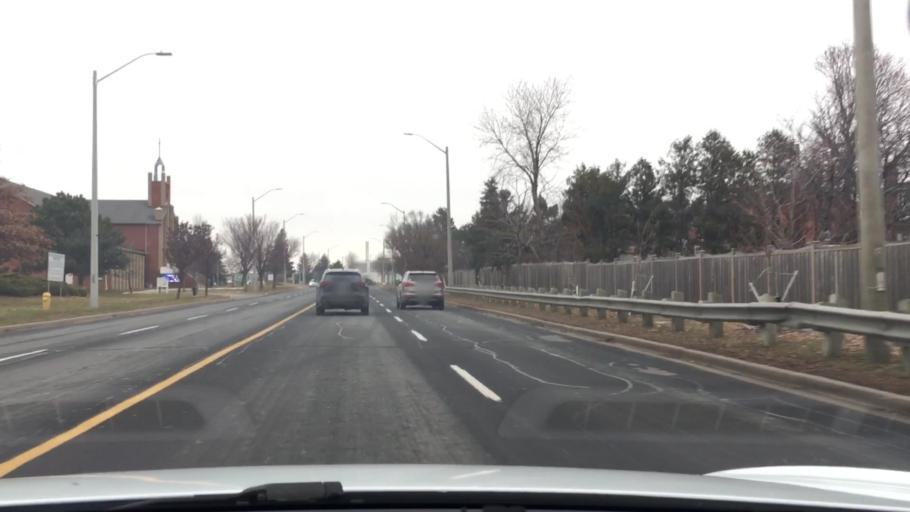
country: CA
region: Ontario
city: Markham
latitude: 43.8290
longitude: -79.3235
